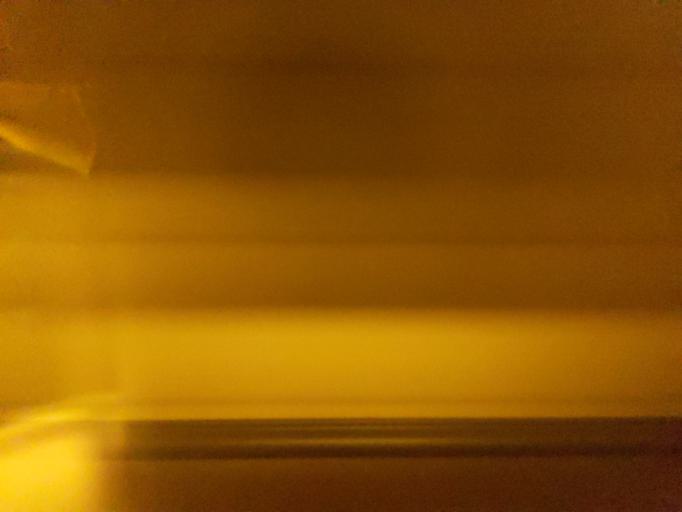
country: JP
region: Miyagi
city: Shiroishi
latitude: 38.0020
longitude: 140.6385
